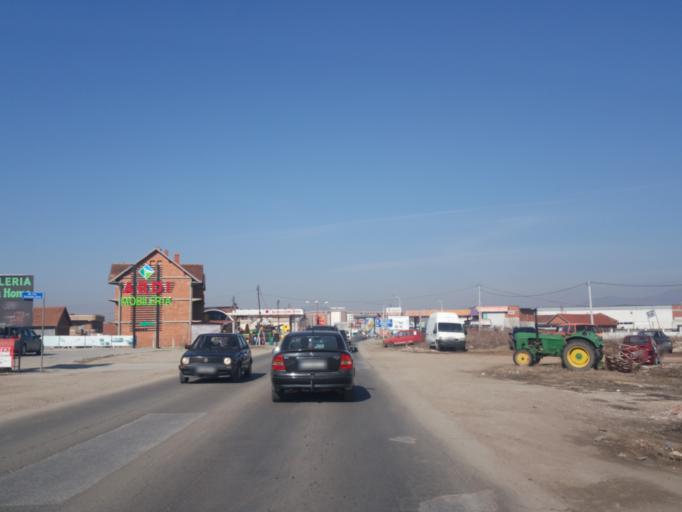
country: XK
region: Mitrovica
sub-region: Vushtrri
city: Vushtrri
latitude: 42.8126
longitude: 20.9851
